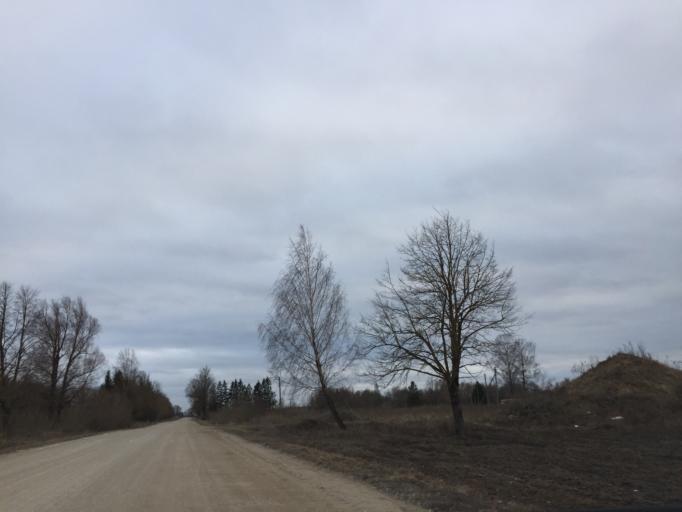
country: LT
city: Zagare
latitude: 56.3530
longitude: 23.2554
